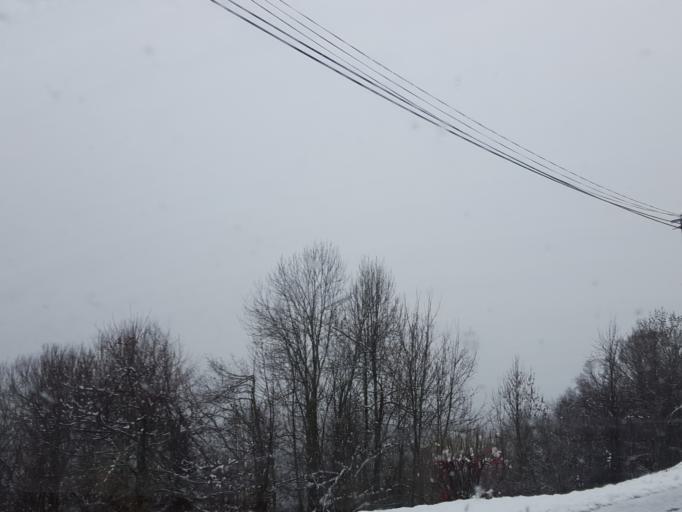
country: FR
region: Midi-Pyrenees
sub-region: Departement de l'Ariege
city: Montjoie-en-Couserans
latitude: 42.9048
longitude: 1.3503
